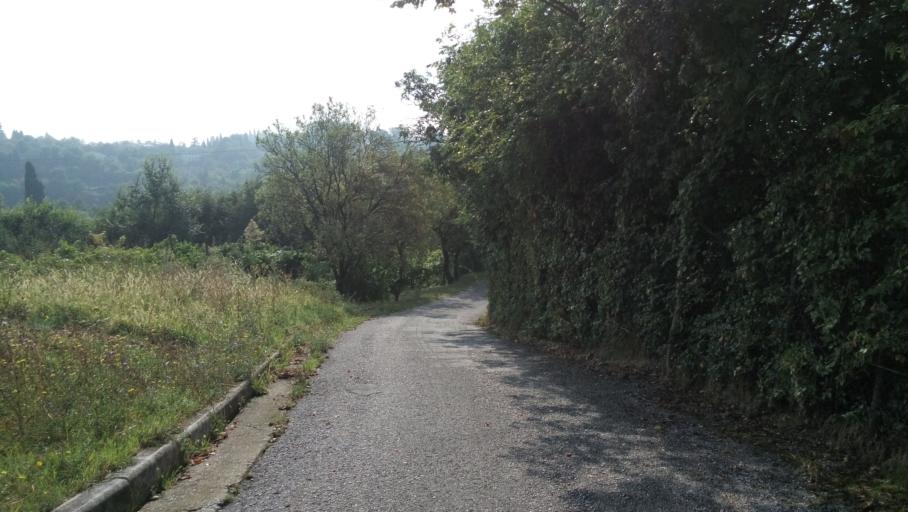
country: IT
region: Veneto
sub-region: Provincia di Vicenza
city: Monteviale
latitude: 45.5423
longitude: 11.4567
